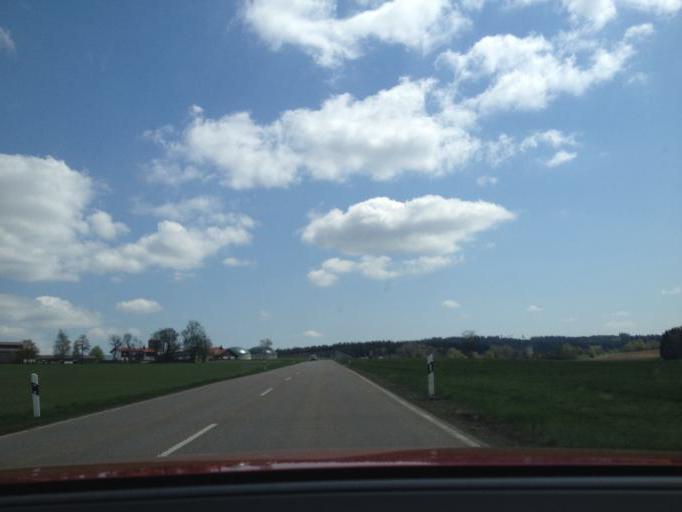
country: DE
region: Bavaria
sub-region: Upper Palatinate
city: Waldershof
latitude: 49.9793
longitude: 12.0875
